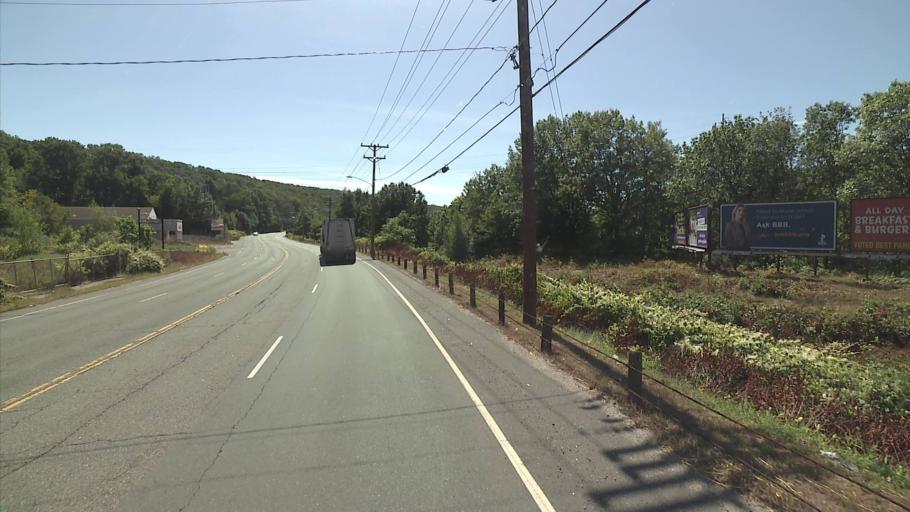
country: US
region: Connecticut
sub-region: New Haven County
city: Waterbury
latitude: 41.5261
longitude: -73.0409
